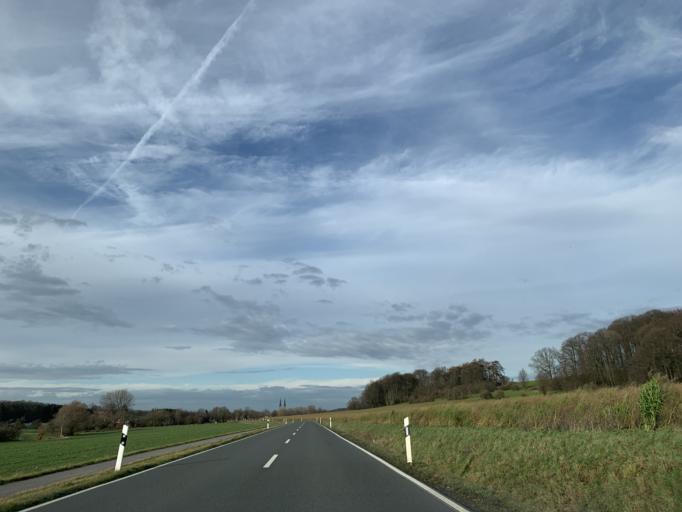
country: DE
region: North Rhine-Westphalia
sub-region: Regierungsbezirk Munster
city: Billerbeck
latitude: 51.9610
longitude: 7.3139
